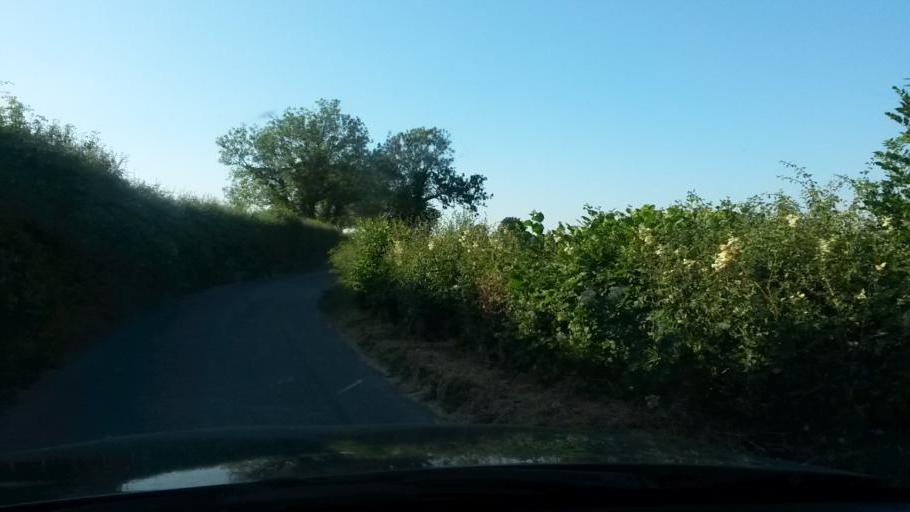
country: IE
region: Leinster
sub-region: Fingal County
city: Swords
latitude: 53.5005
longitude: -6.2914
